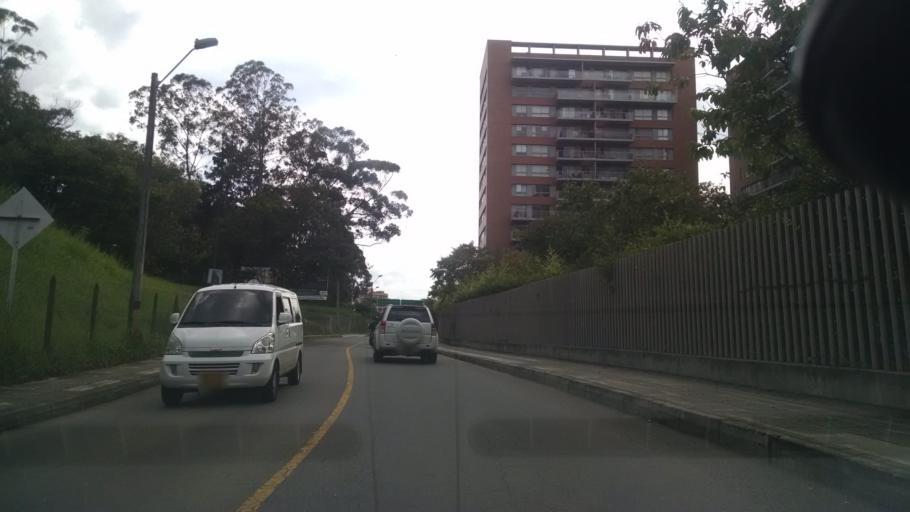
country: CO
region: Antioquia
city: Envigado
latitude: 6.1956
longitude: -75.5707
